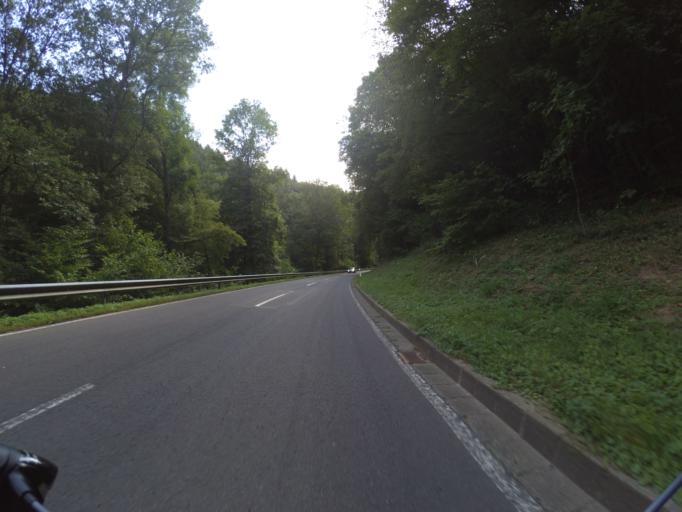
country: DE
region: Rheinland-Pfalz
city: Heidenburg
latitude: 49.8012
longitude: 6.9017
